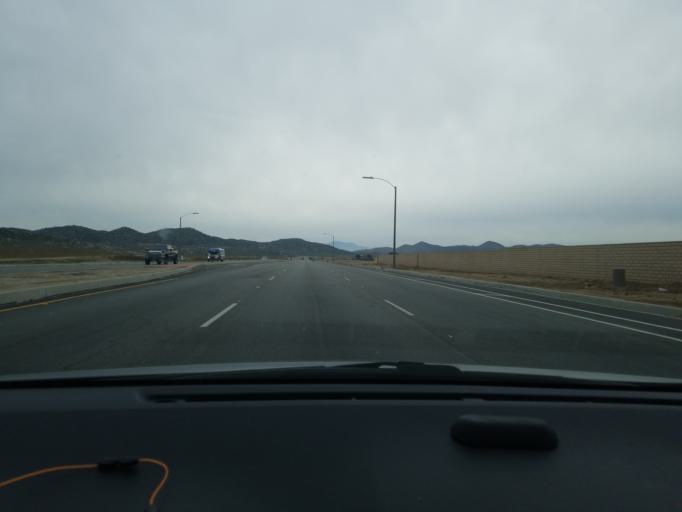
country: US
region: California
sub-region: Riverside County
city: Winchester
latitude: 33.6926
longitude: -117.1055
